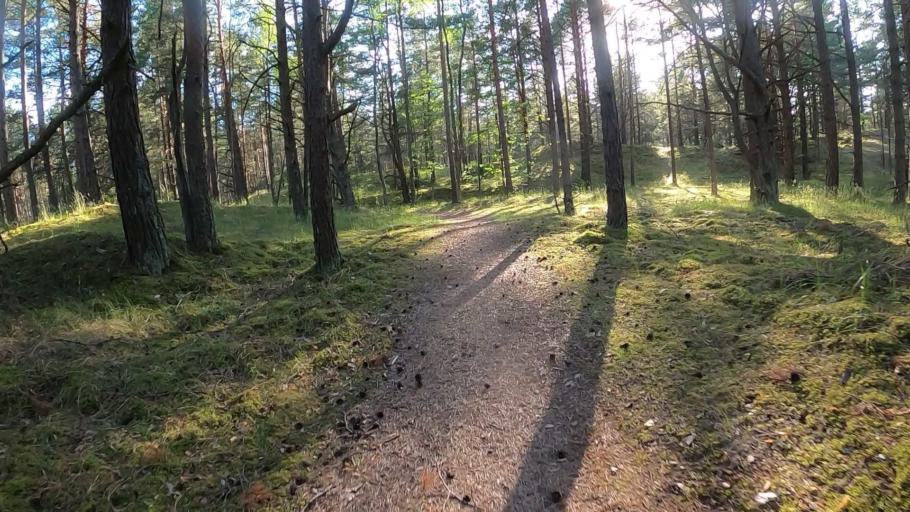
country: LV
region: Carnikava
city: Carnikava
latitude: 57.1338
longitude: 24.2316
